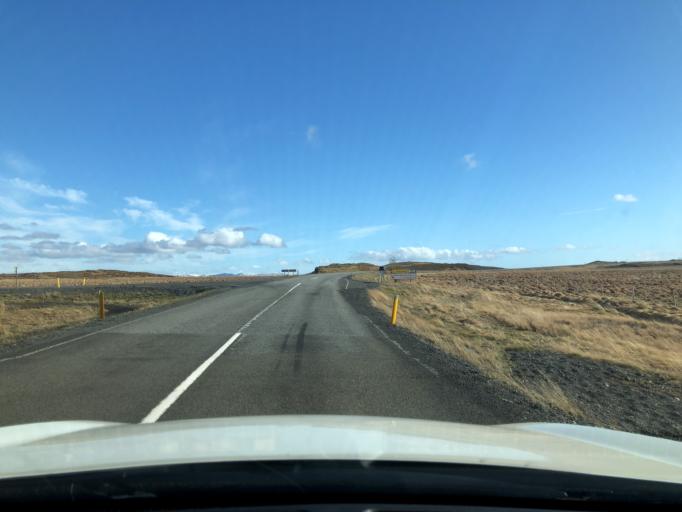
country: IS
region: West
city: Borgarnes
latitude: 64.5557
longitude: -21.7319
